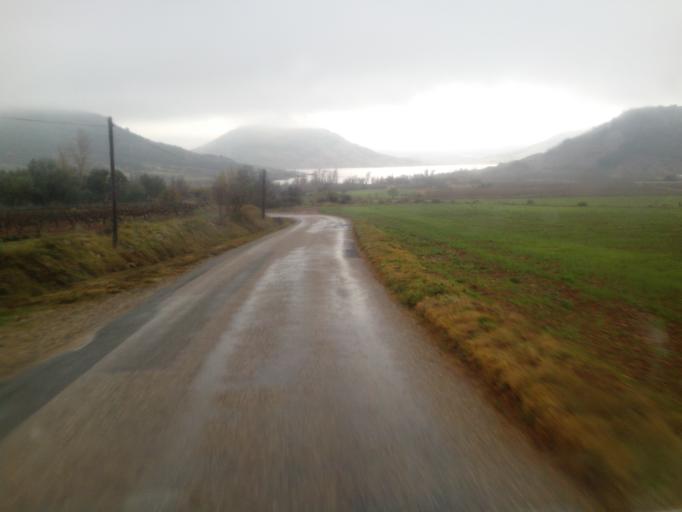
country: FR
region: Languedoc-Roussillon
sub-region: Departement de l'Herault
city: Nebian
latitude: 43.6421
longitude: 3.3556
